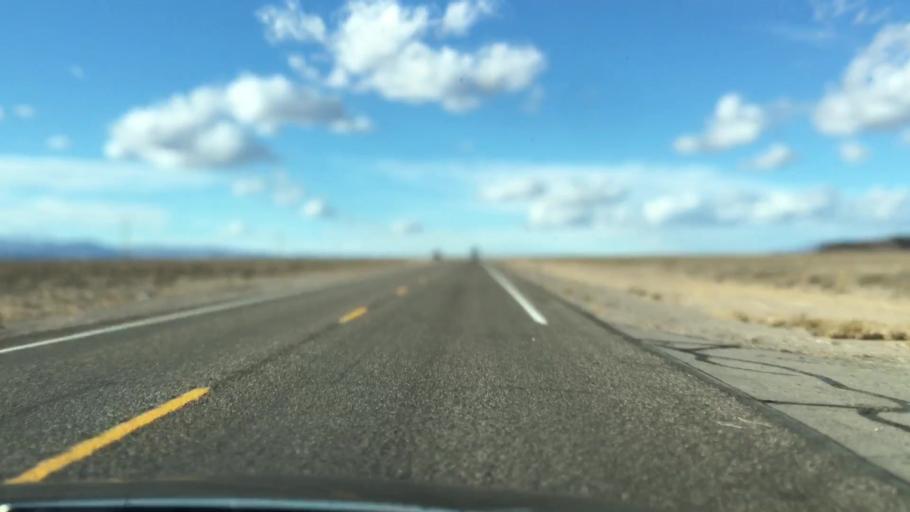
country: US
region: Nevada
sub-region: Nye County
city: Beatty
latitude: 37.1934
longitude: -116.9465
